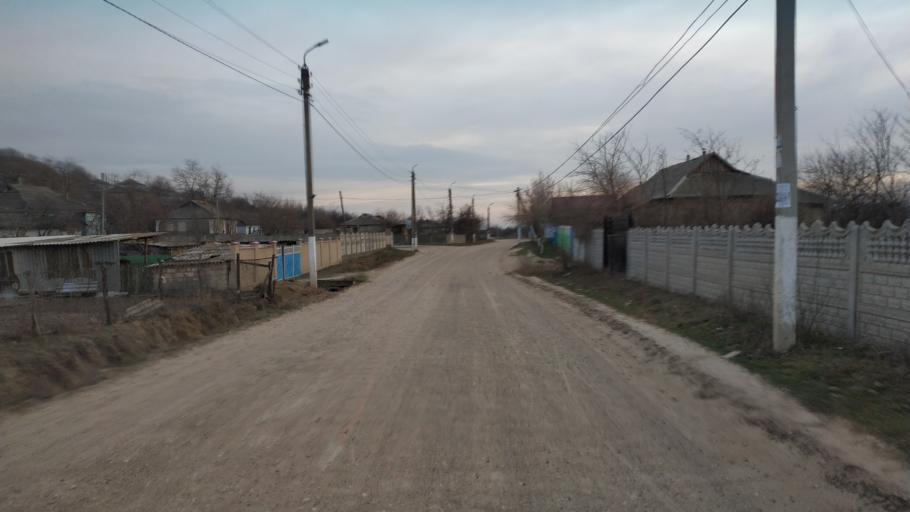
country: MD
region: Hincesti
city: Dancu
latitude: 46.7517
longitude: 28.2064
